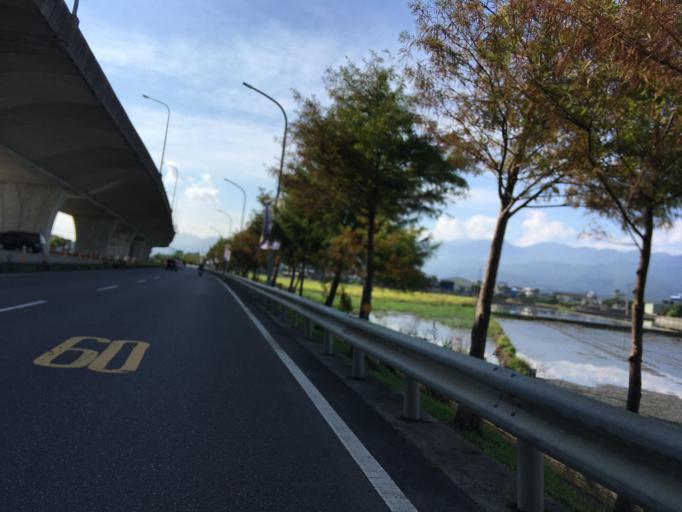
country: TW
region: Taiwan
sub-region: Yilan
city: Yilan
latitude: 24.6698
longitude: 121.7960
